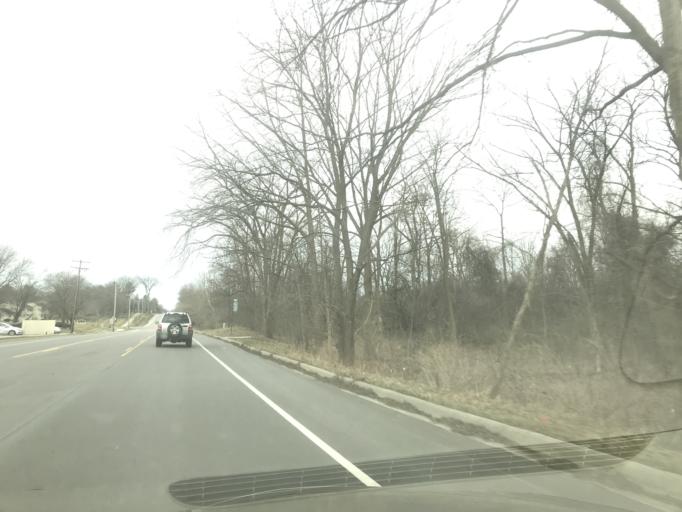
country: US
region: Michigan
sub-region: Ingham County
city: Haslett
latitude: 42.7555
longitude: -84.4213
